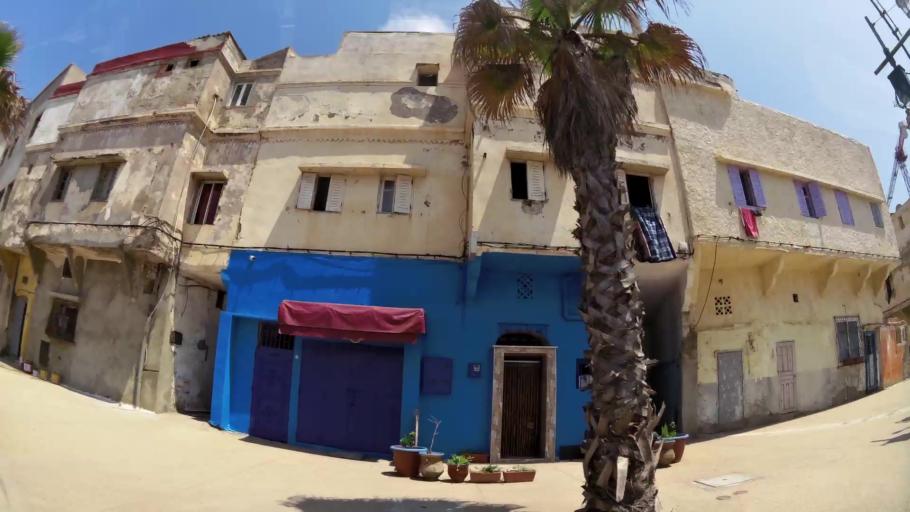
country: MA
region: Rabat-Sale-Zemmour-Zaer
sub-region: Rabat
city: Rabat
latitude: 34.0129
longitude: -6.8633
